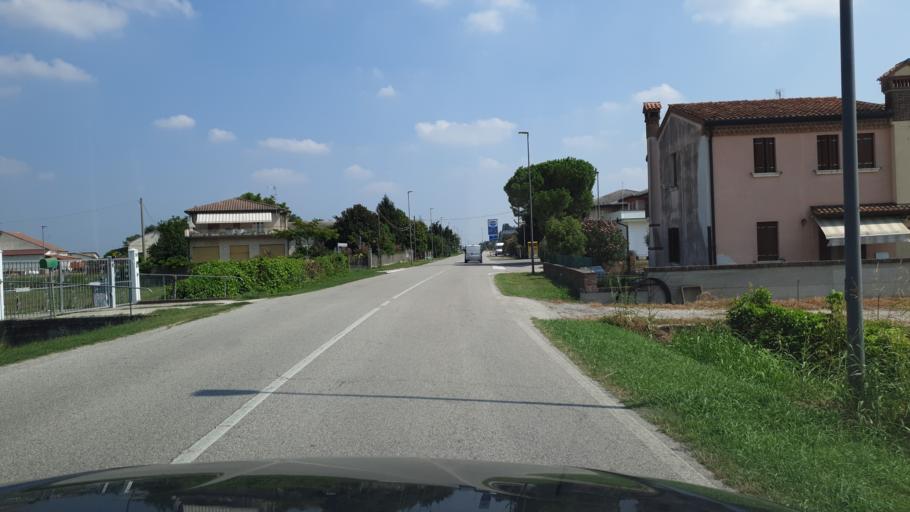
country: IT
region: Veneto
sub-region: Provincia di Rovigo
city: Arqua Polesine
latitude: 45.0129
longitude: 11.7382
